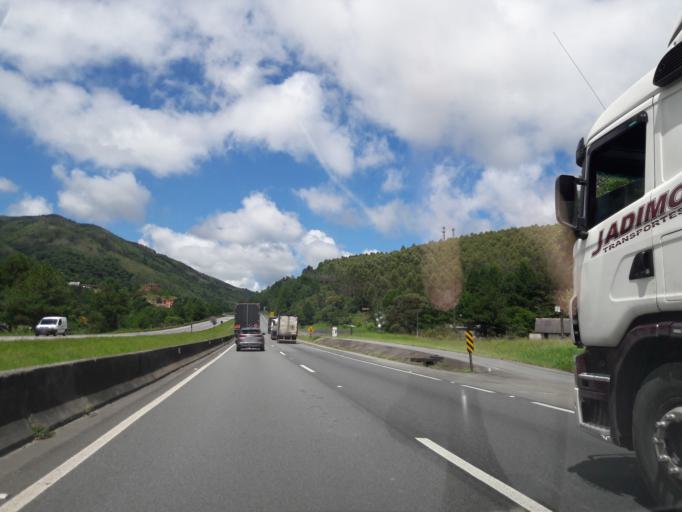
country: BR
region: Parana
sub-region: Campina Grande Do Sul
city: Campina Grande do Sul
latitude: -25.1306
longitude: -48.8574
